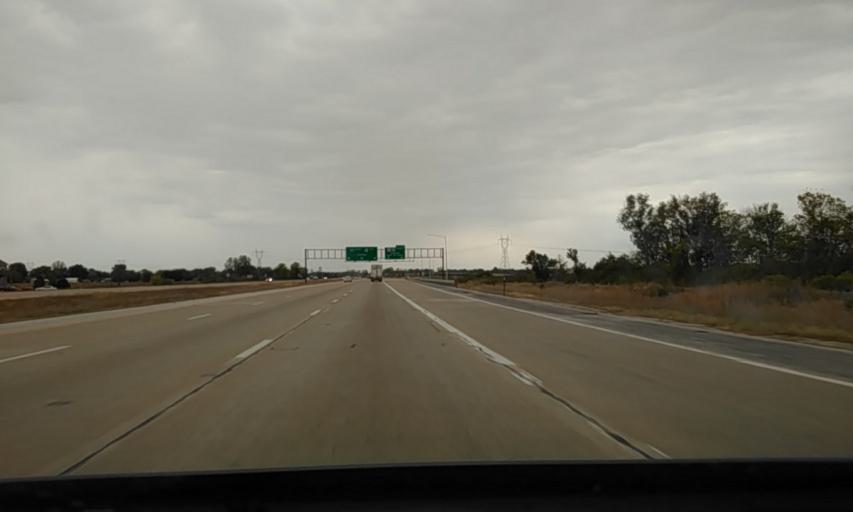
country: US
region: Illinois
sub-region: Saint Clair County
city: Dupo
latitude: 38.5173
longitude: -90.2000
